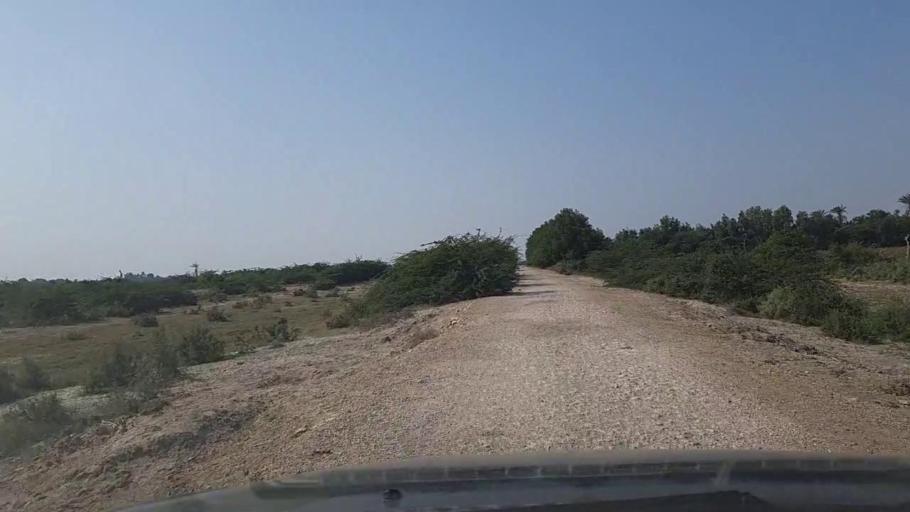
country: PK
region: Sindh
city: Mirpur Sakro
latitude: 24.4060
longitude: 67.6783
